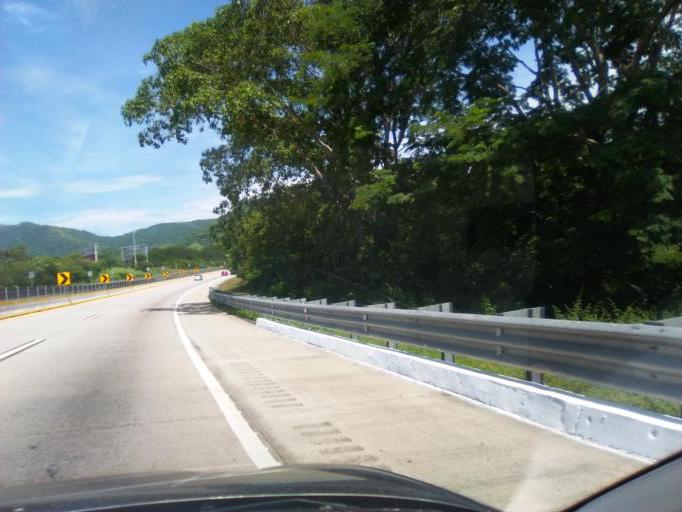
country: MX
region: Guerrero
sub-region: Acapulco de Juarez
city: Kilometro 30
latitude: 16.9952
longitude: -99.6980
